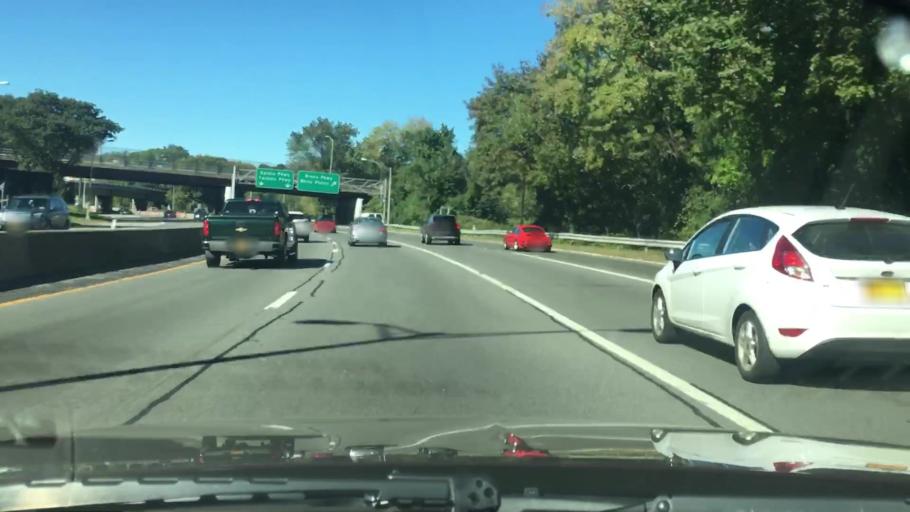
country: US
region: New York
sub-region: Westchester County
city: Bronxville
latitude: 40.9363
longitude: -73.8365
